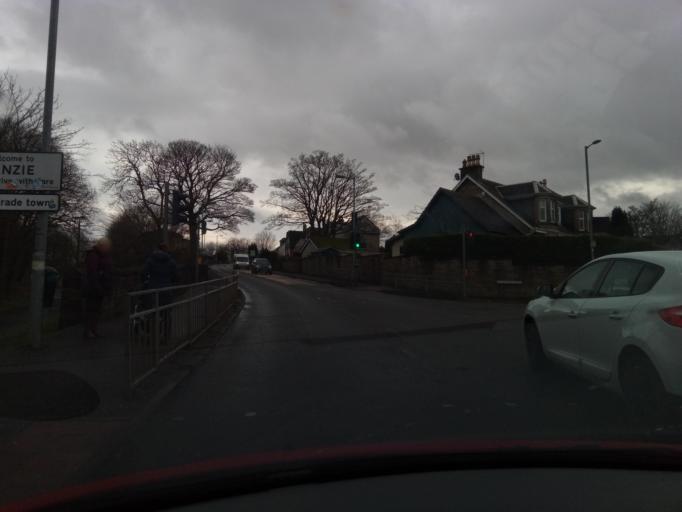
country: GB
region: Scotland
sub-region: East Dunbartonshire
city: Kirkintilloch
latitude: 55.9315
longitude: -4.1536
